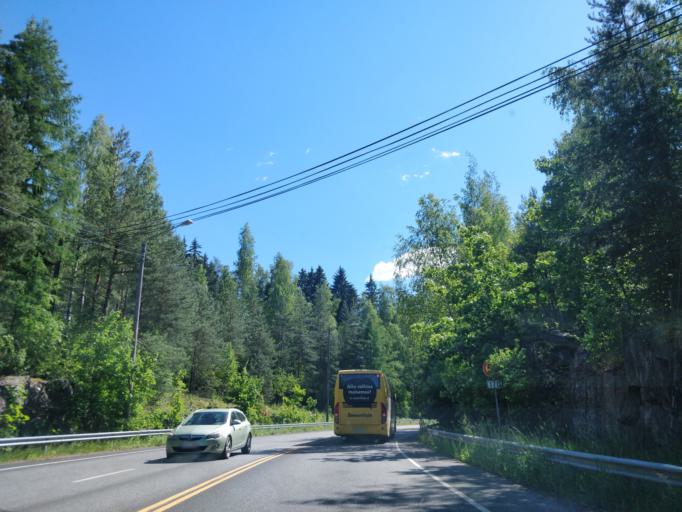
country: FI
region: Uusimaa
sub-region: Porvoo
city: Porvoo
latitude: 60.3900
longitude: 25.6339
